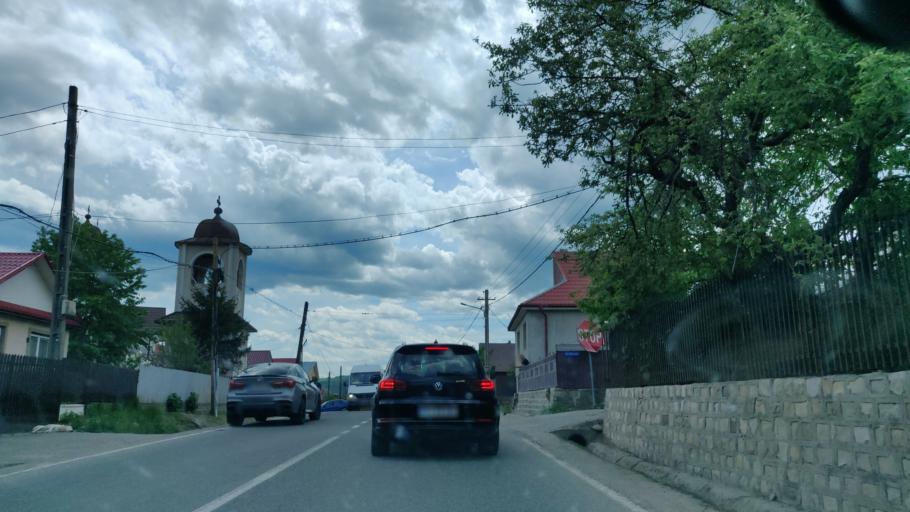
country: RO
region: Vrancea
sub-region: Comuna Tulnici
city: Tulnici
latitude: 45.9217
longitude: 26.6750
